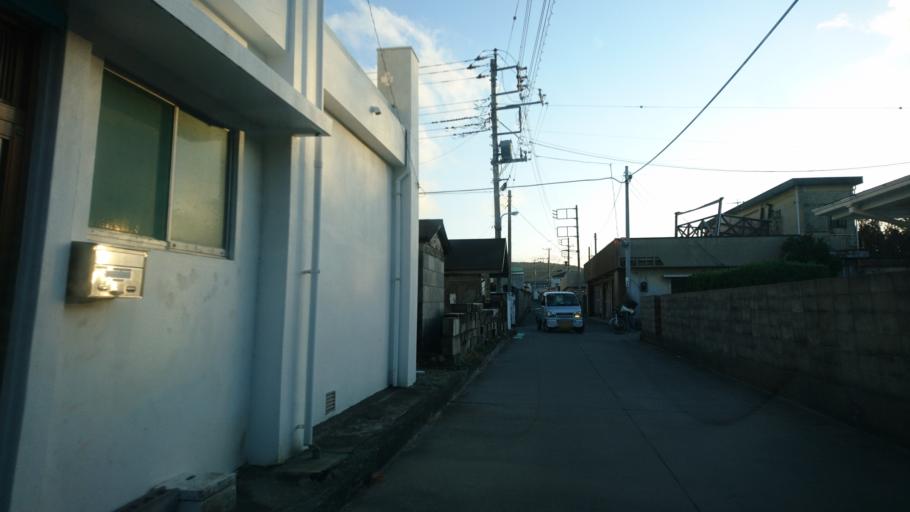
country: JP
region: Shizuoka
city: Shimoda
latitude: 34.3792
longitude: 139.2549
